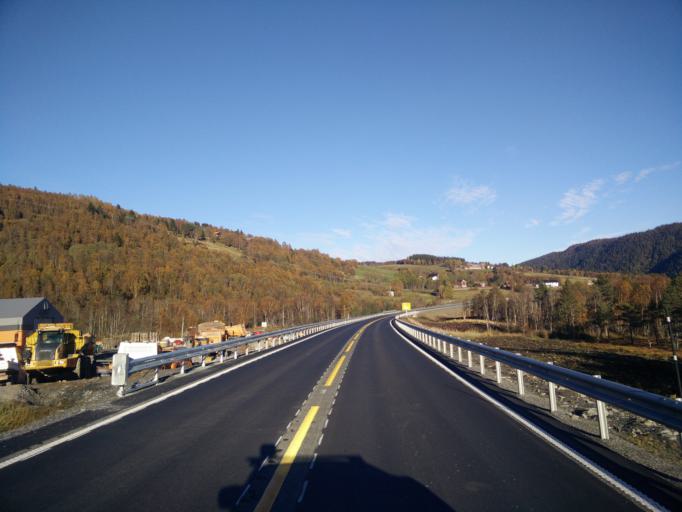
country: NO
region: Sor-Trondelag
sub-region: Snillfjord
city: Krokstadora
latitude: 63.2849
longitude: 9.6164
